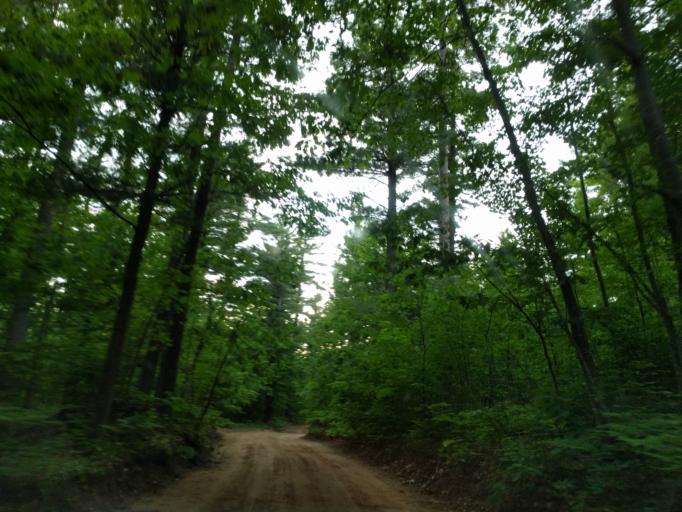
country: US
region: Michigan
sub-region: Marquette County
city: Trowbridge Park
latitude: 46.6053
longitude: -87.5038
